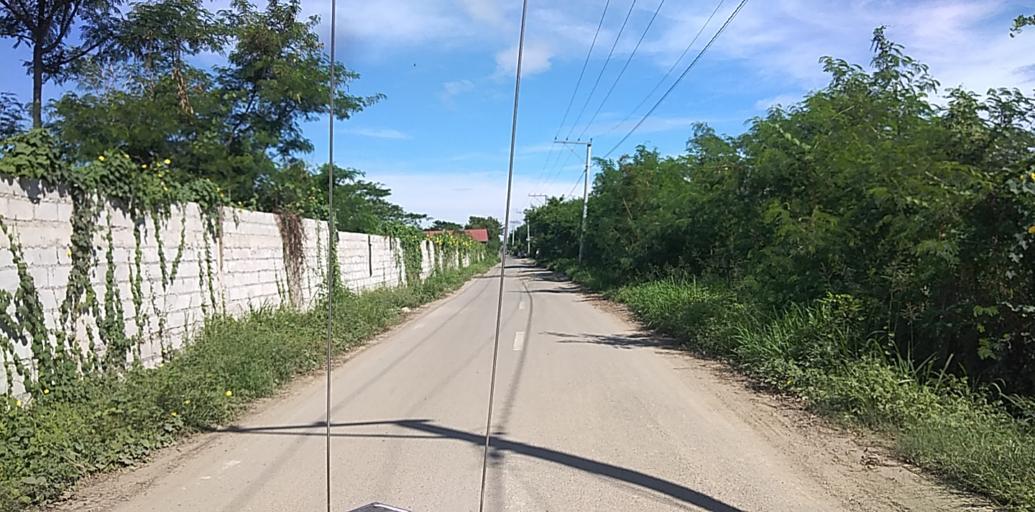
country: PH
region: Central Luzon
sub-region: Province of Pampanga
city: Candaba
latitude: 15.0771
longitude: 120.8078
